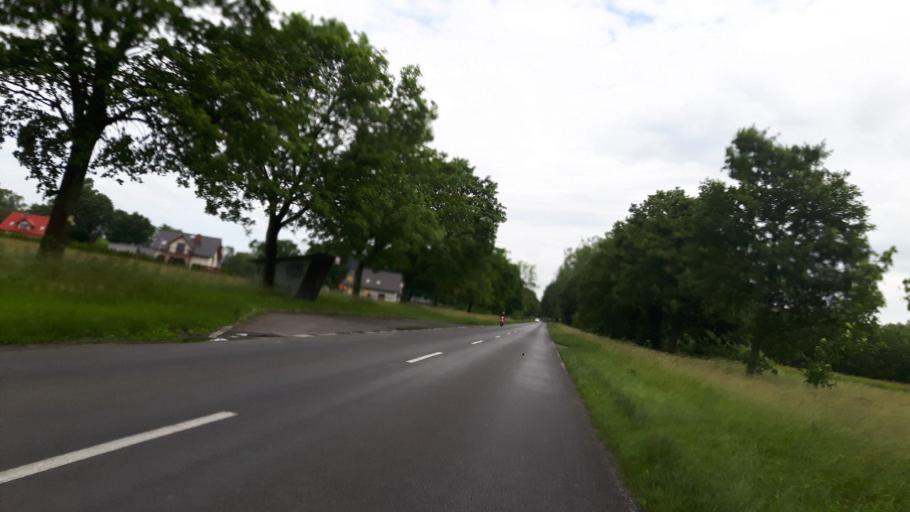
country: PL
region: West Pomeranian Voivodeship
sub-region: Powiat gryficki
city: Gryfice
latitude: 53.9405
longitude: 15.2193
